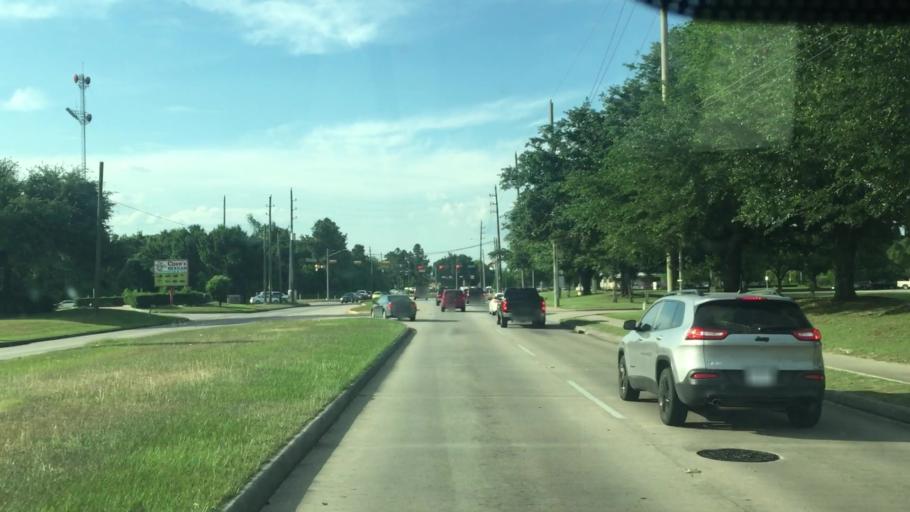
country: US
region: Texas
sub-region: Harris County
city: Hudson
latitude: 29.9598
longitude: -95.4985
